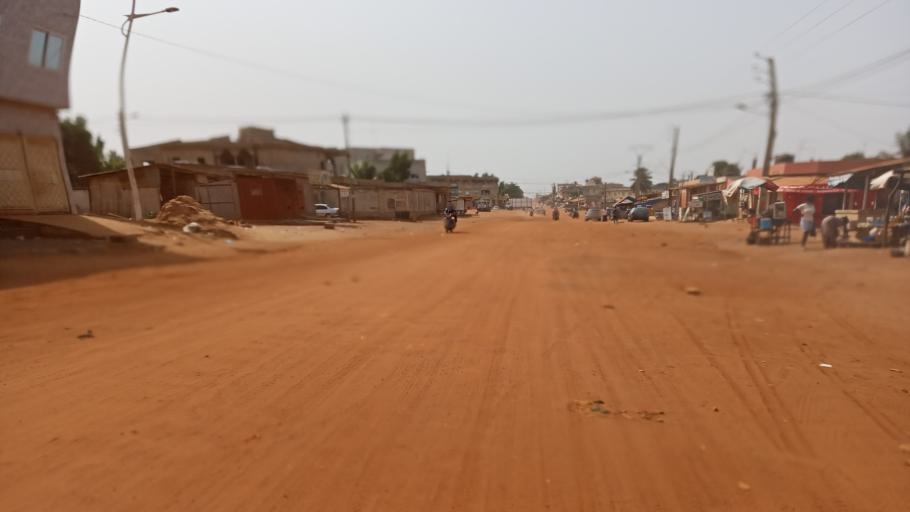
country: TG
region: Maritime
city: Lome
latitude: 6.2031
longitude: 1.1667
